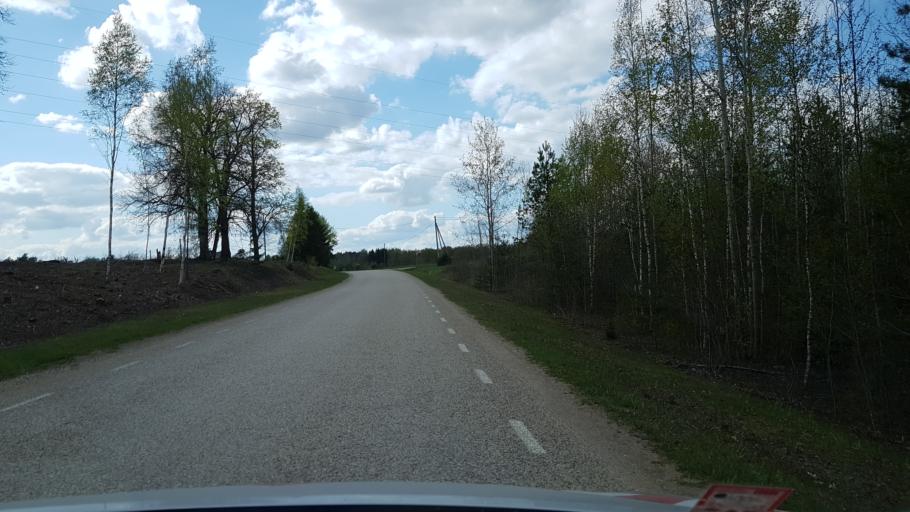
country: EE
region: Tartu
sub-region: UElenurme vald
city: Ulenurme
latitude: 58.3444
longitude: 26.8253
